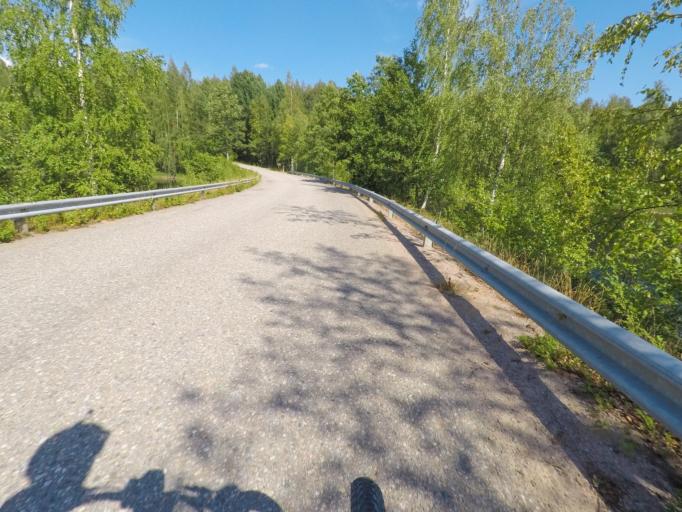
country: FI
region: Southern Savonia
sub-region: Mikkeli
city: Puumala
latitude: 61.4198
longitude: 28.1178
